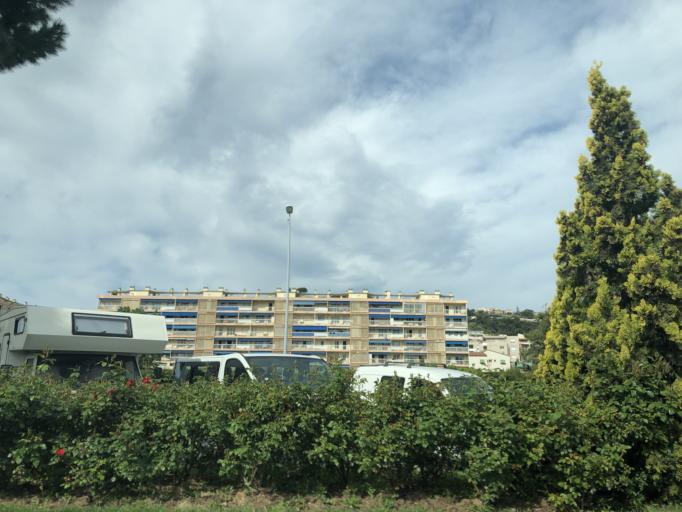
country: FR
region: Provence-Alpes-Cote d'Azur
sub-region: Departement des Alpes-Maritimes
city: Saint-Laurent-du-Var
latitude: 43.6813
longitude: 7.1897
